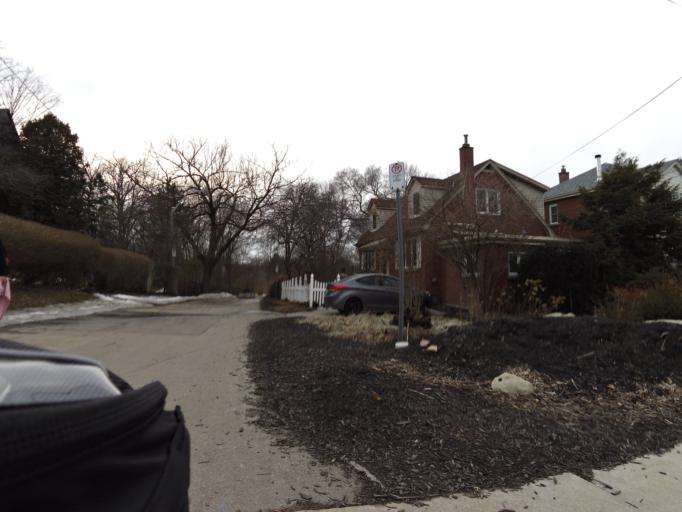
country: CA
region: Ontario
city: Hamilton
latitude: 43.2505
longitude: -79.8973
